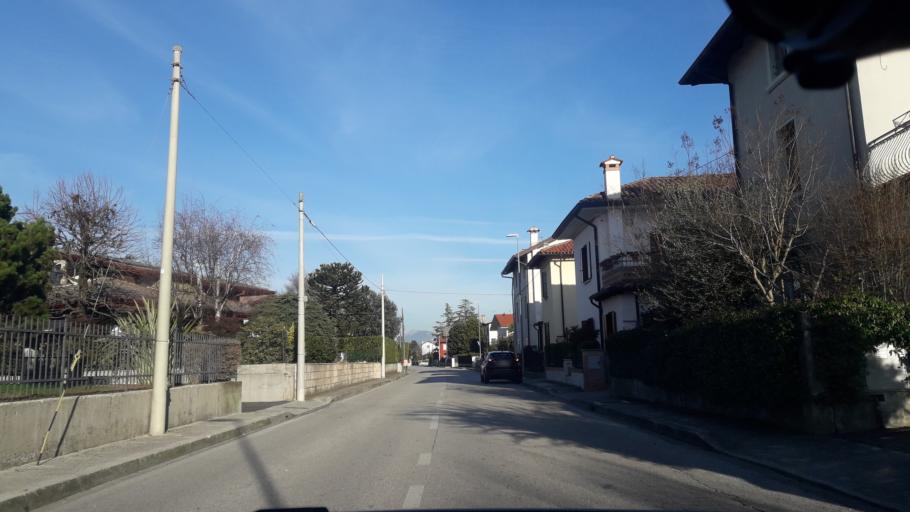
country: IT
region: Friuli Venezia Giulia
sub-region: Provincia di Udine
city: Passons
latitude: 46.0732
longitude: 13.1857
